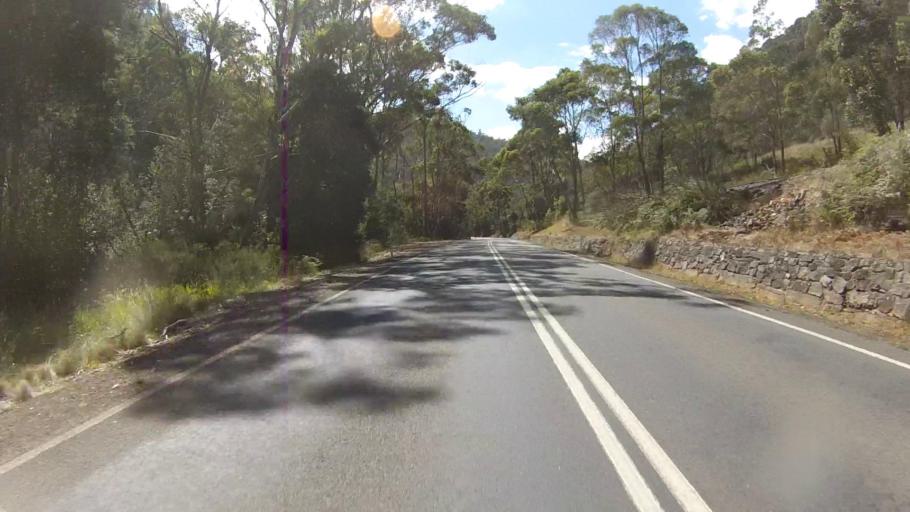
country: AU
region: Tasmania
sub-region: Derwent Valley
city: New Norfolk
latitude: -42.6796
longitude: 146.7532
